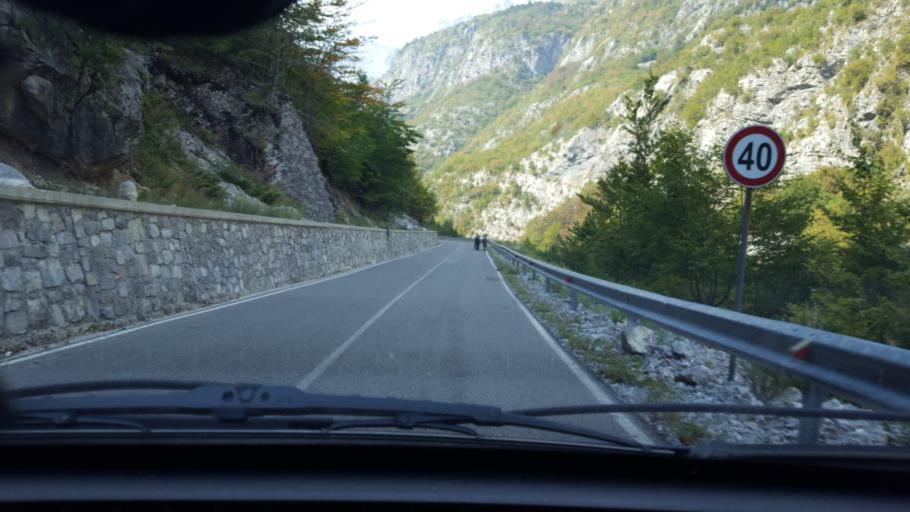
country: ME
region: Andrijevica
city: Andrijevica
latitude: 42.5330
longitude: 19.6655
